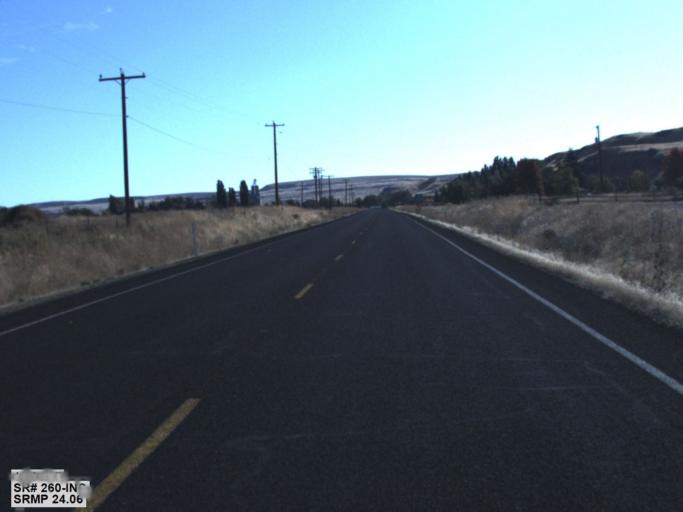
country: US
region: Washington
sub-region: Franklin County
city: Connell
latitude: 46.6444
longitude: -118.5718
